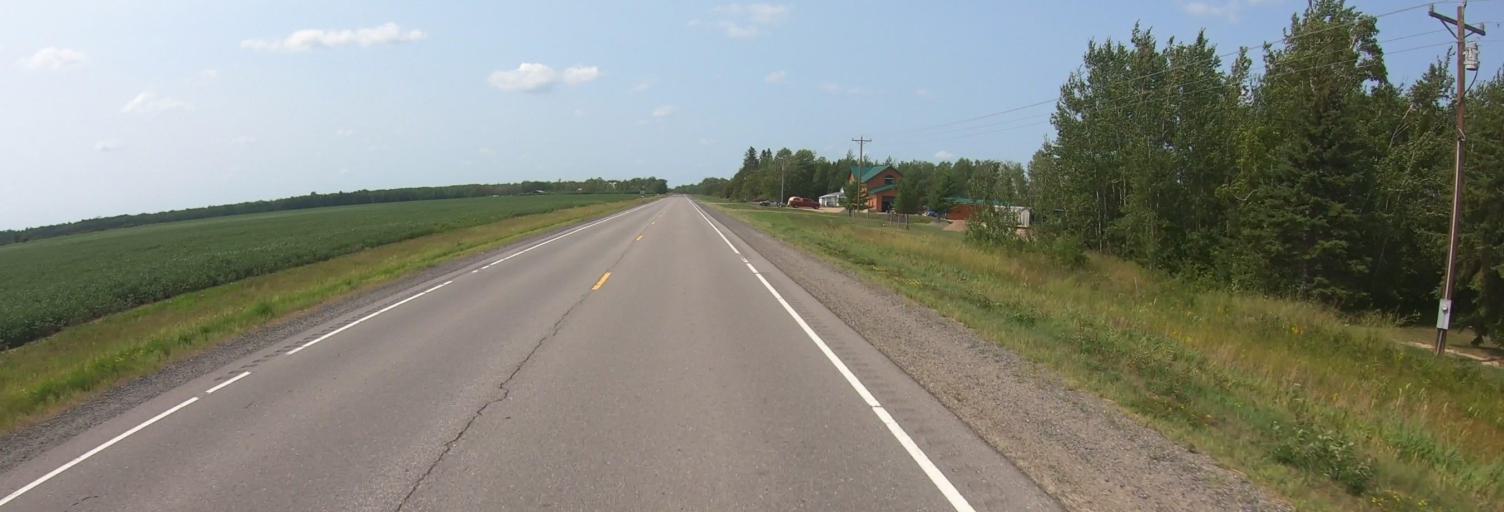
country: US
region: Minnesota
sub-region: Lake of the Woods County
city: Baudette
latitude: 48.6915
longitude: -94.4582
